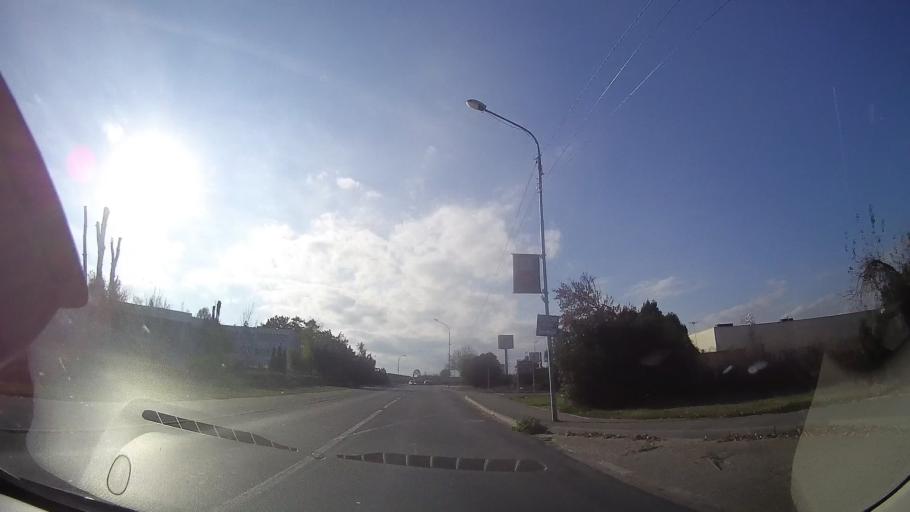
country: RO
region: Constanta
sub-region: Municipiul Mangalia
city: Mangalia
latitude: 43.8297
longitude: 28.5829
